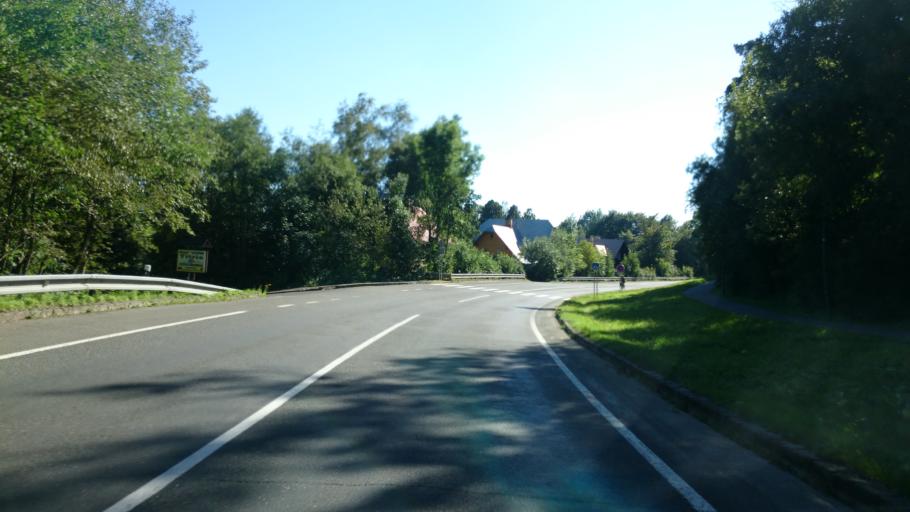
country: SK
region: Presovsky
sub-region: Okres Poprad
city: Nova Lesna
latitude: 49.1691
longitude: 20.2864
